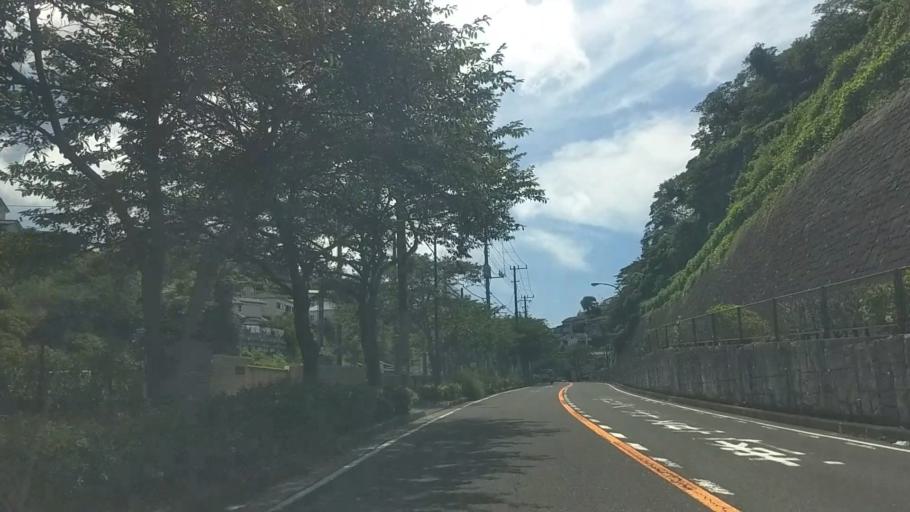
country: JP
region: Kanagawa
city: Yokosuka
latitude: 35.2755
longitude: 139.6502
